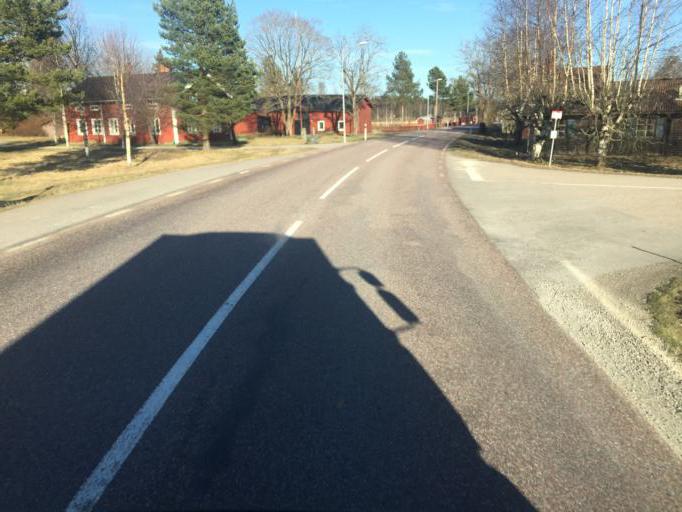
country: SE
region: Dalarna
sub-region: Vansbro Kommun
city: Jarna
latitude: 60.4490
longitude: 14.5128
